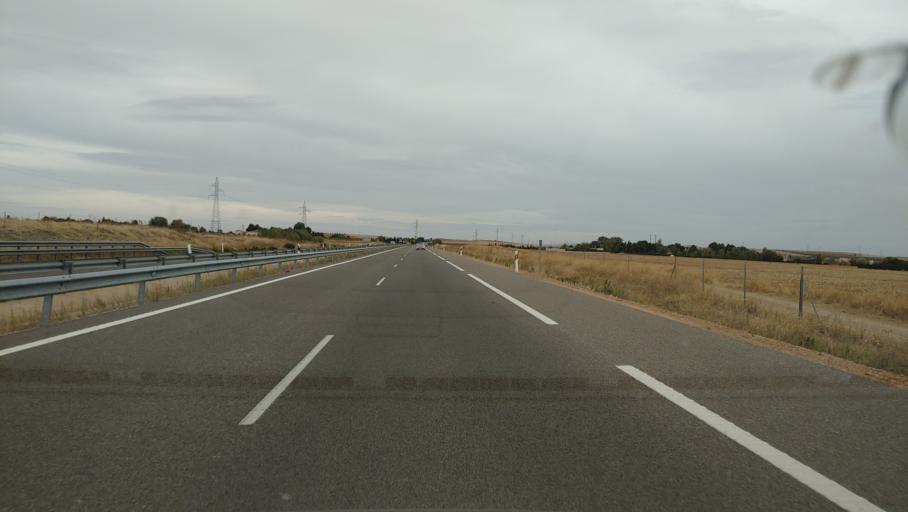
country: ES
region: Castille-La Mancha
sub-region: Provincia de Ciudad Real
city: Miguelturra
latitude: 38.9491
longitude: -3.9063
